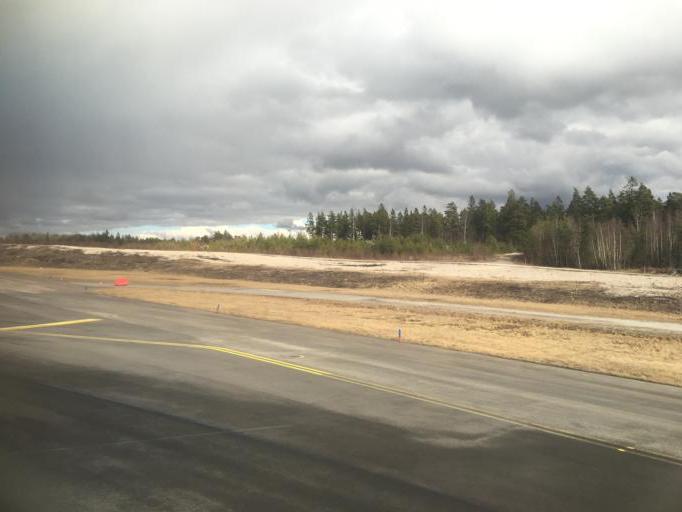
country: SE
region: Stockholm
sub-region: Sigtuna Kommun
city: Marsta
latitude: 59.6643
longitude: 17.9266
